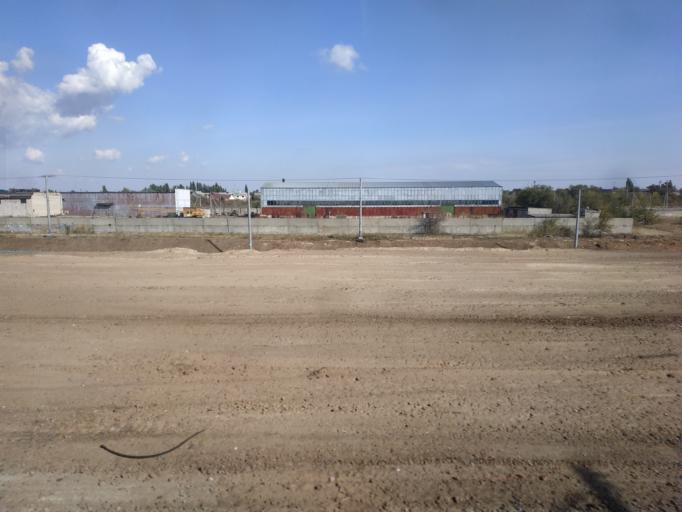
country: RU
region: Volgograd
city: Gumrak
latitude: 48.7715
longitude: 44.3878
